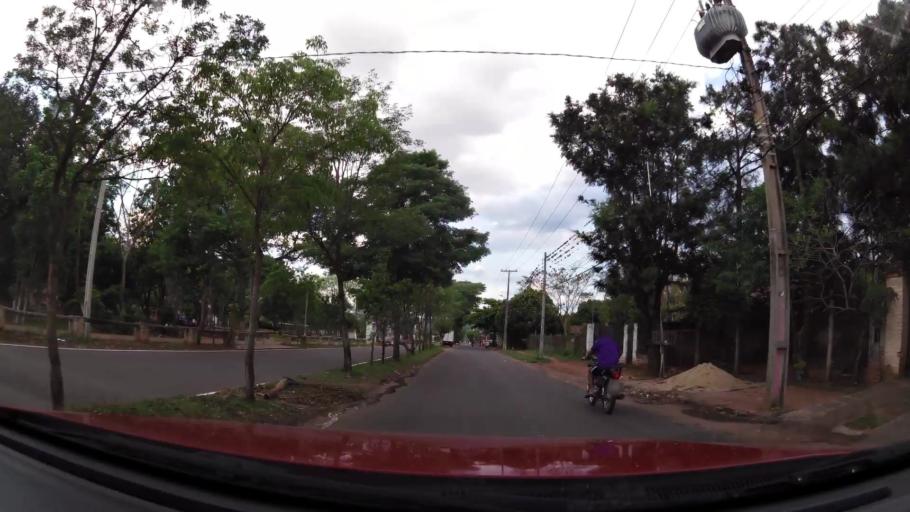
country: PY
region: Central
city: Nemby
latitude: -25.3687
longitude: -57.5564
